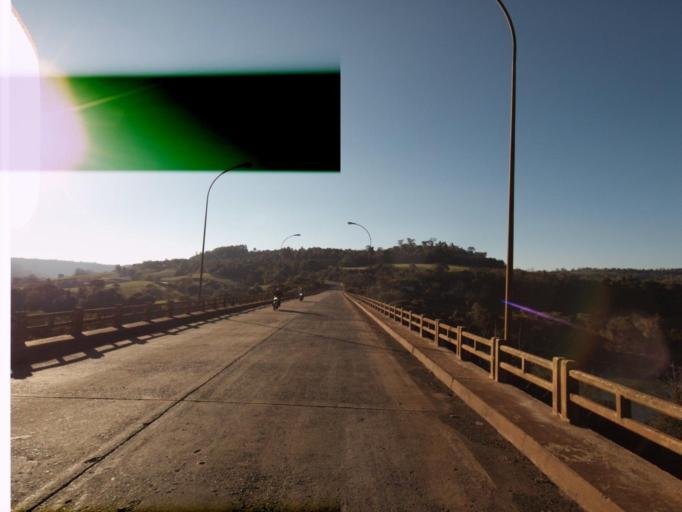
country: BR
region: Santa Catarina
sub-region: Chapeco
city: Chapeco
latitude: -26.9264
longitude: -52.8565
